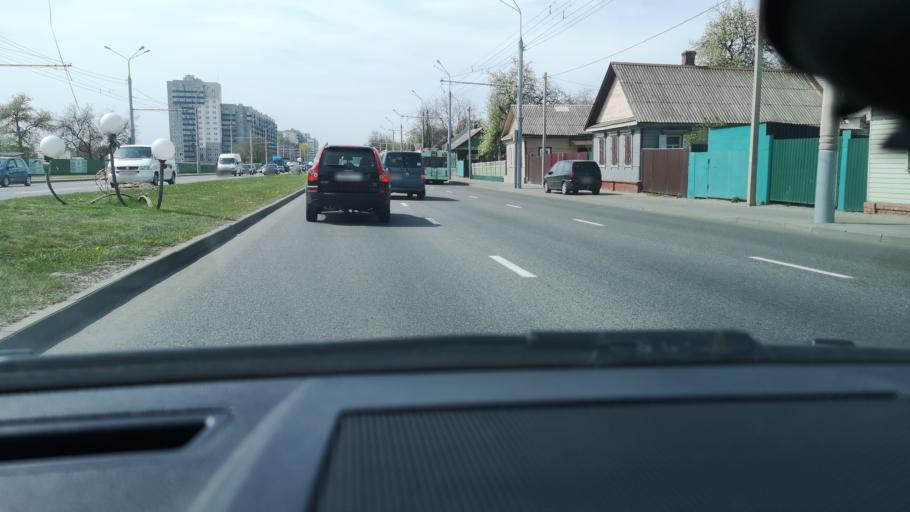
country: BY
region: Gomel
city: Gomel
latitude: 52.4172
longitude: 30.9909
